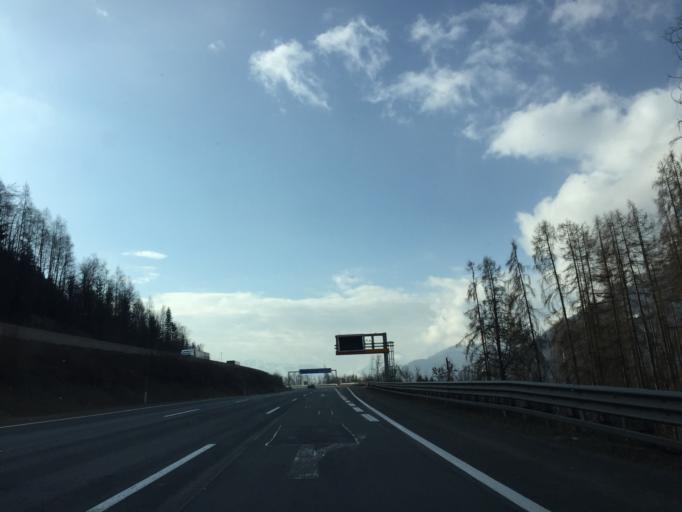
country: AT
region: Salzburg
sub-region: Politischer Bezirk Sankt Johann im Pongau
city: Pfarrwerfen
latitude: 47.4488
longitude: 13.2180
